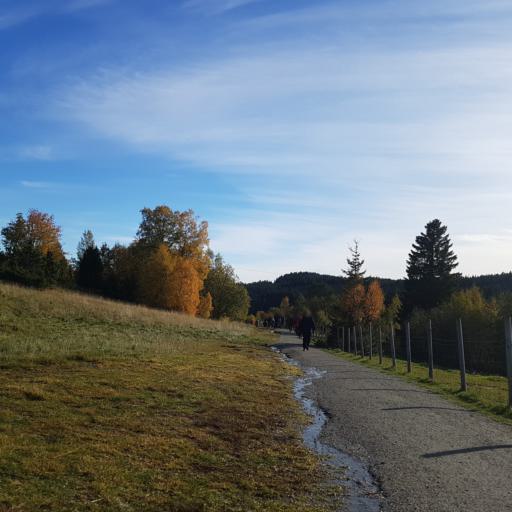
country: NO
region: Sor-Trondelag
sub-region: Trondheim
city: Trondheim
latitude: 63.4219
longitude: 10.3061
